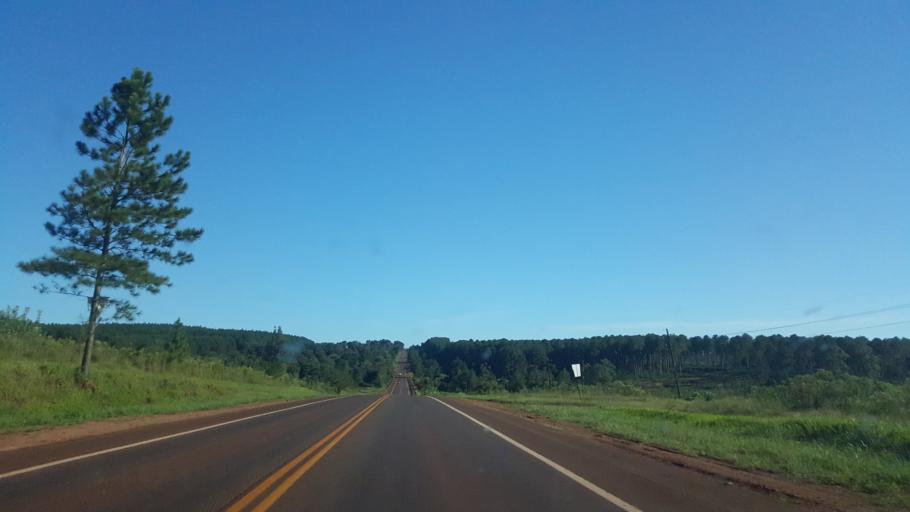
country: AR
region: Misiones
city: Puerto Esperanza
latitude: -26.1473
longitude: -54.5826
